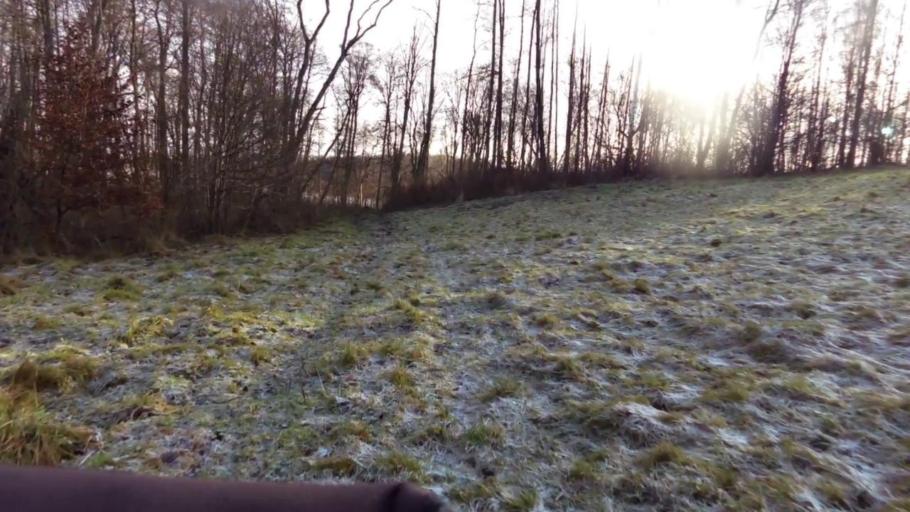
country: PL
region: West Pomeranian Voivodeship
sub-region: Powiat lobeski
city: Wegorzyno
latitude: 53.5345
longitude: 15.6739
